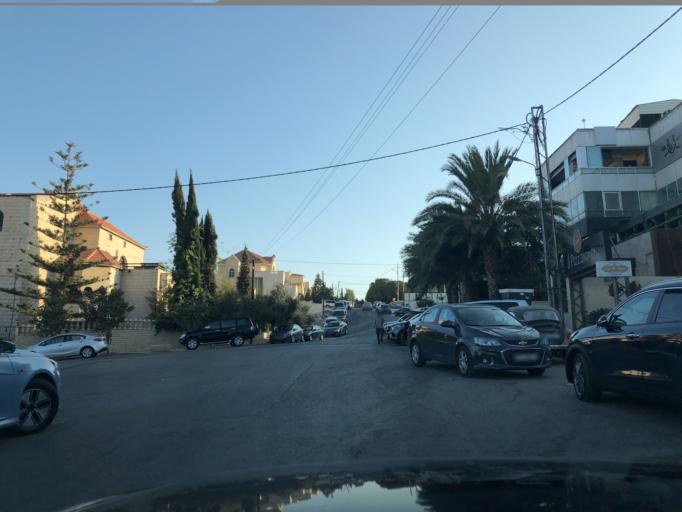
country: JO
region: Amman
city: Al Bunayyat ash Shamaliyah
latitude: 31.9404
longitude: 35.8848
